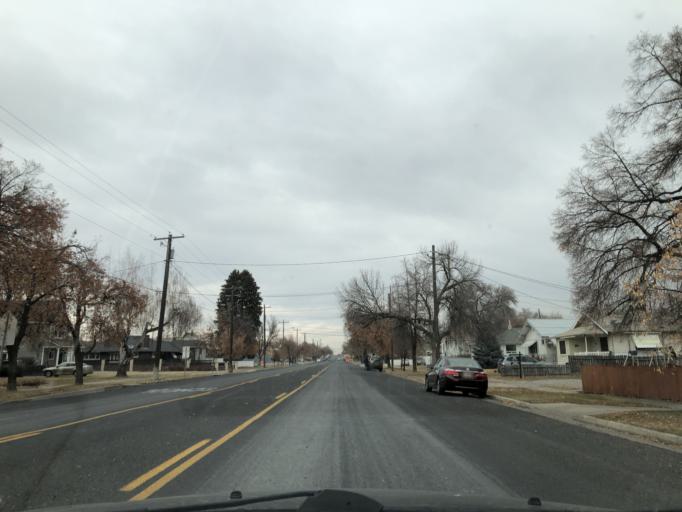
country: US
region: Utah
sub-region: Cache County
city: Logan
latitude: 41.7246
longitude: -111.8378
